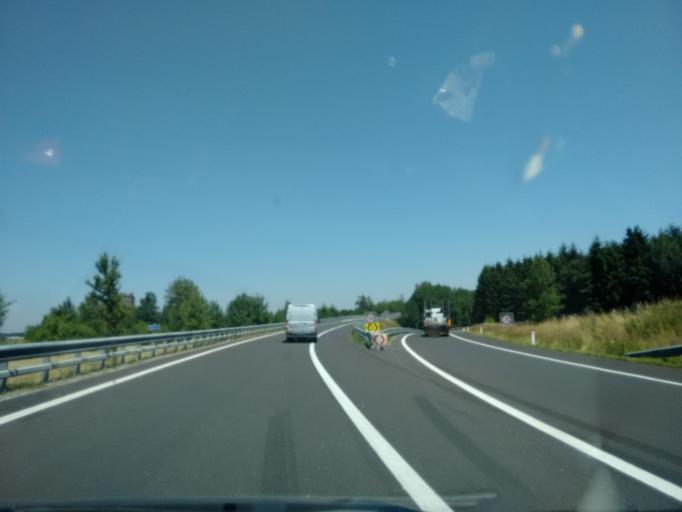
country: AT
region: Upper Austria
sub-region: Wels-Land
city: Sattledt
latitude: 48.0610
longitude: 14.0374
